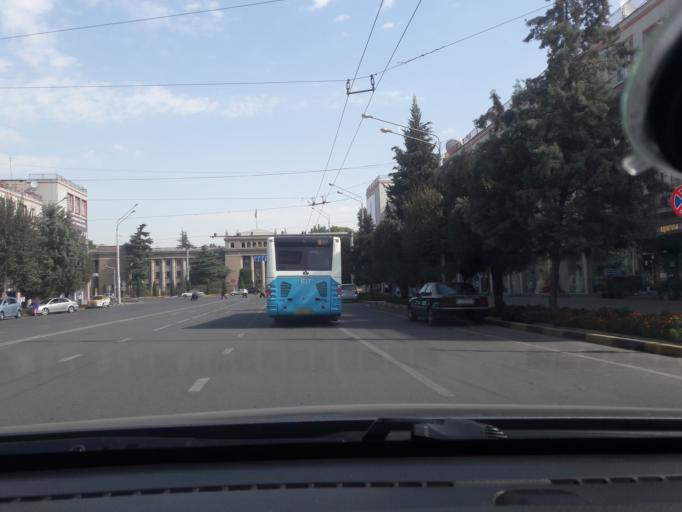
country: TJ
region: Dushanbe
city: Dushanbe
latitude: 38.5830
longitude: 68.7853
